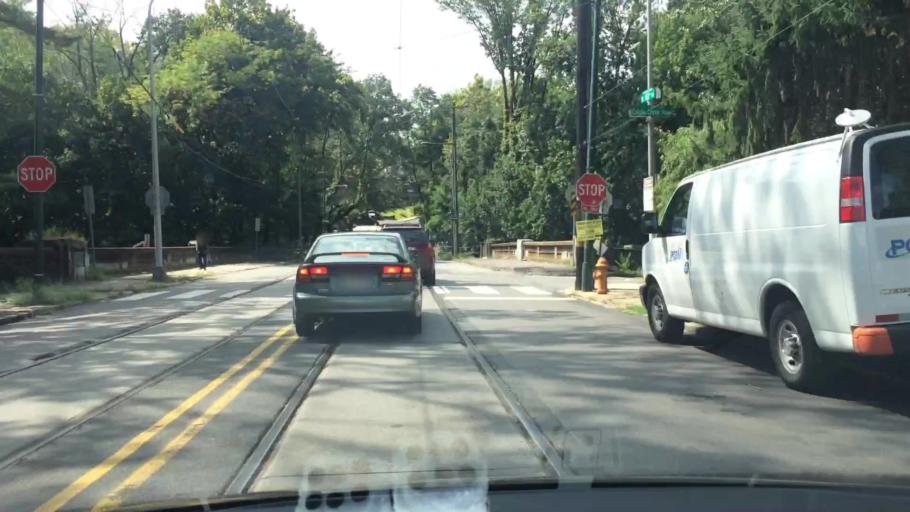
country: US
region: Pennsylvania
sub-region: Delaware County
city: Yeadon
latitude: 39.9294
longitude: -75.2429
